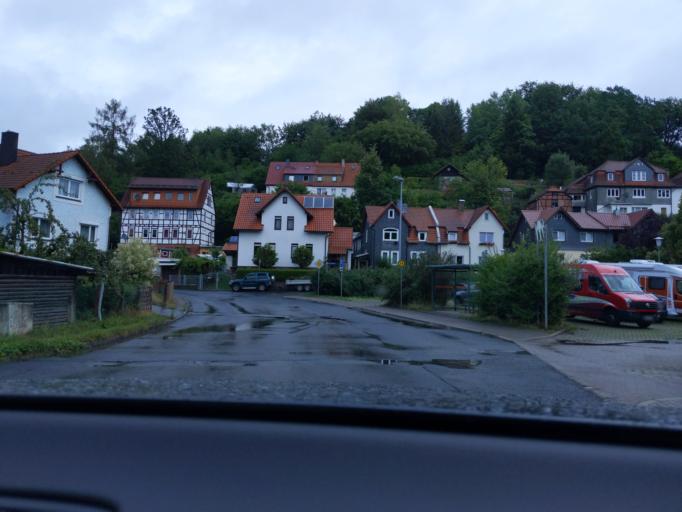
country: DE
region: Thuringia
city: Suhl
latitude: 50.6010
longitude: 10.6564
